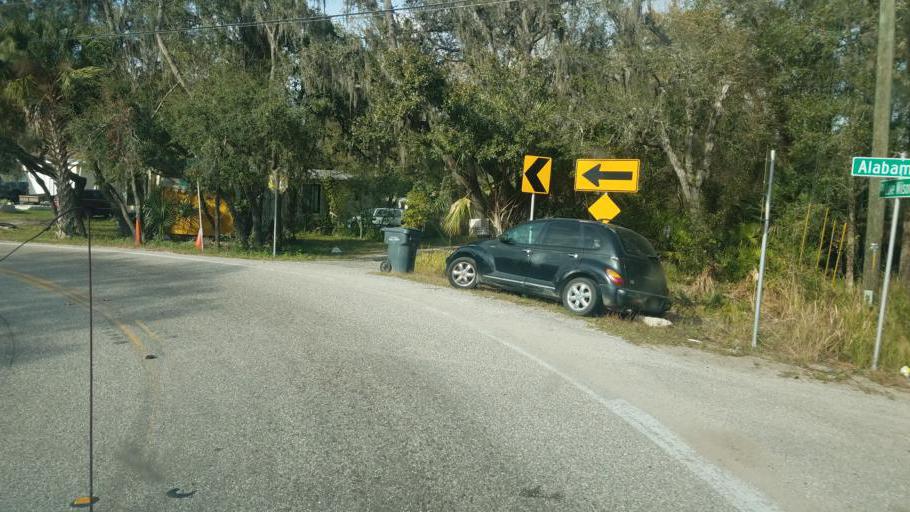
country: US
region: Florida
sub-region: Polk County
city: Loughman
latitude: 28.2474
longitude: -81.5642
